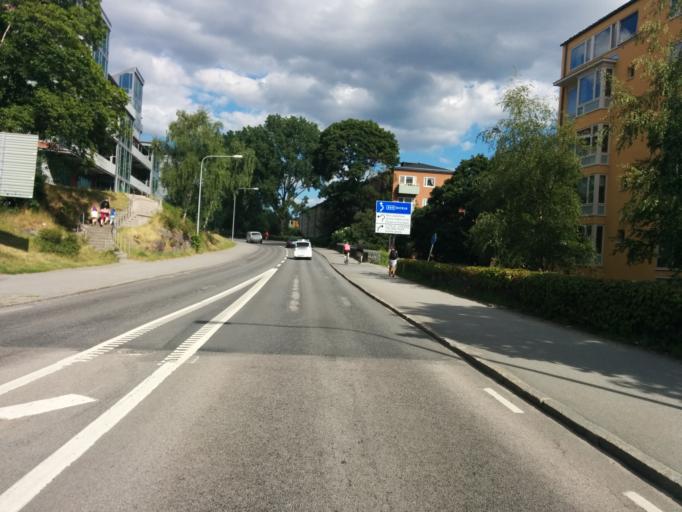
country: SE
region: Stockholm
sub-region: Nacka Kommun
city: Nacka
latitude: 59.3035
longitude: 18.1190
